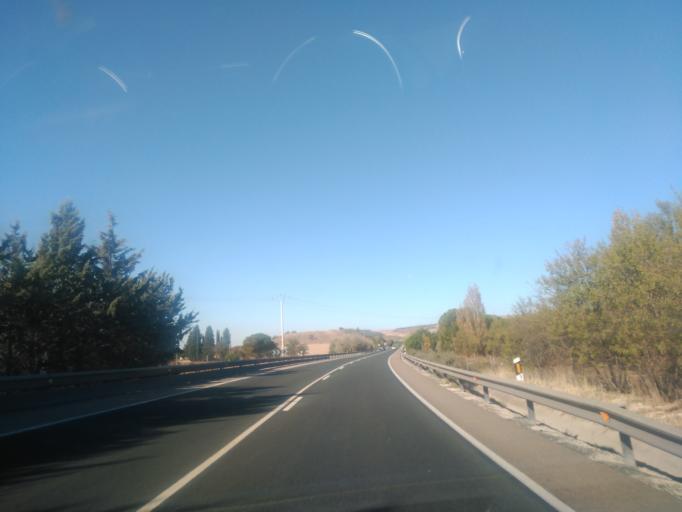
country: ES
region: Castille and Leon
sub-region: Provincia de Valladolid
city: Quintanilla de Onesimo
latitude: 41.6186
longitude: -4.3632
